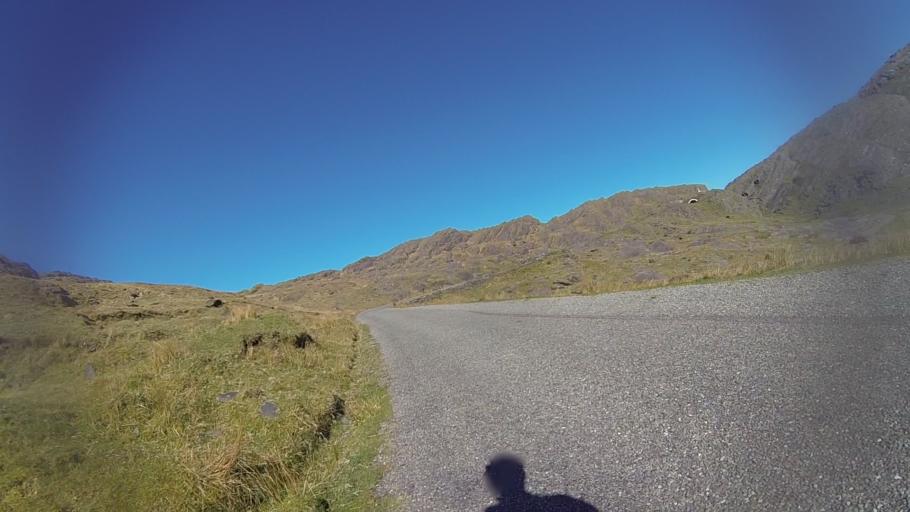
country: IE
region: Munster
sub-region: Ciarrai
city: Kenmare
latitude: 51.7176
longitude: -9.7530
